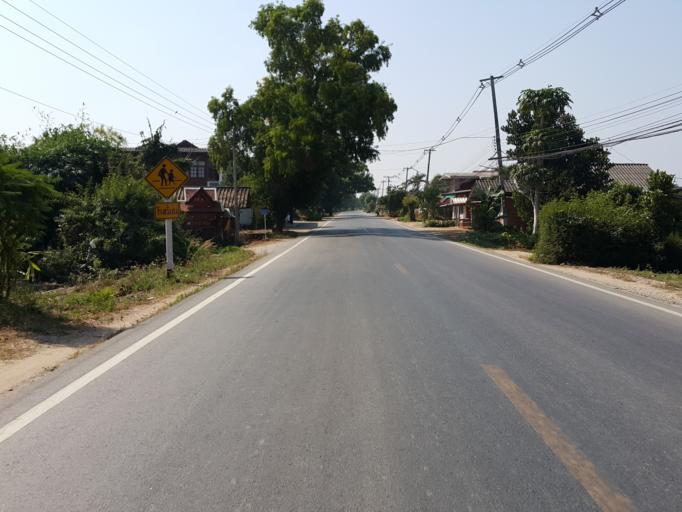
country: TH
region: Lamphun
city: Pa Sang
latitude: 18.4998
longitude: 98.8604
